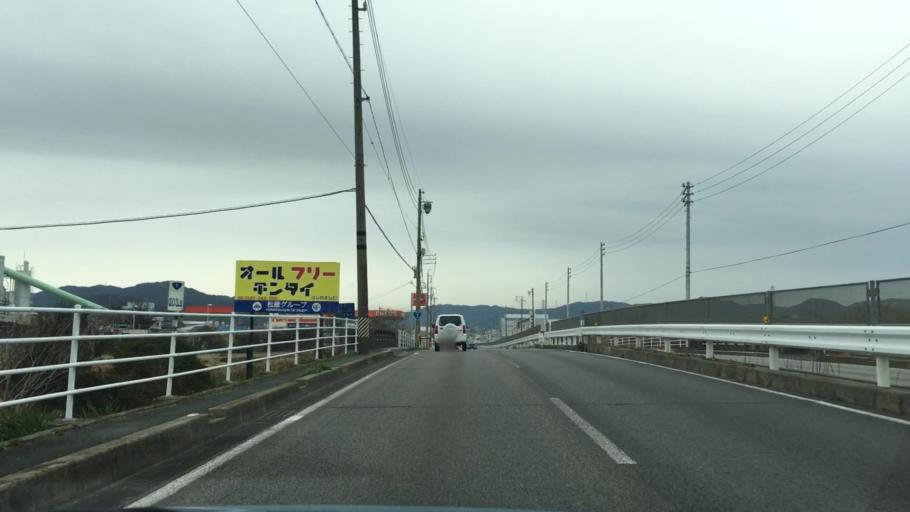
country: JP
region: Aichi
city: Kozakai-cho
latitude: 34.8187
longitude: 137.3478
